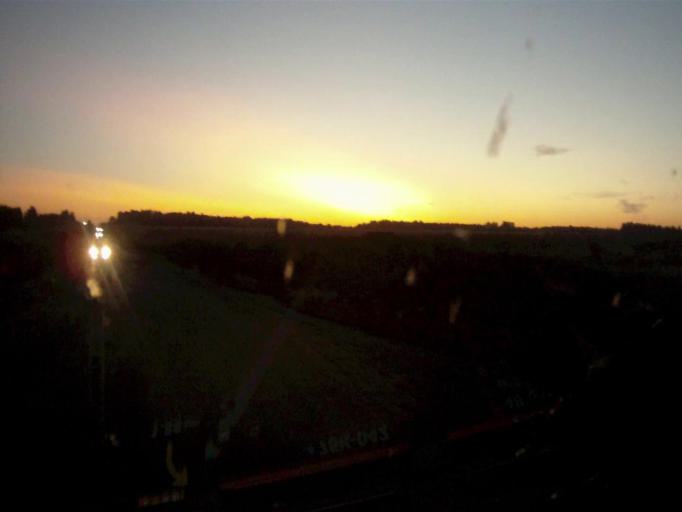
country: RU
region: Chelyabinsk
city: Timiryazevskiy
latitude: 55.2083
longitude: 60.8152
